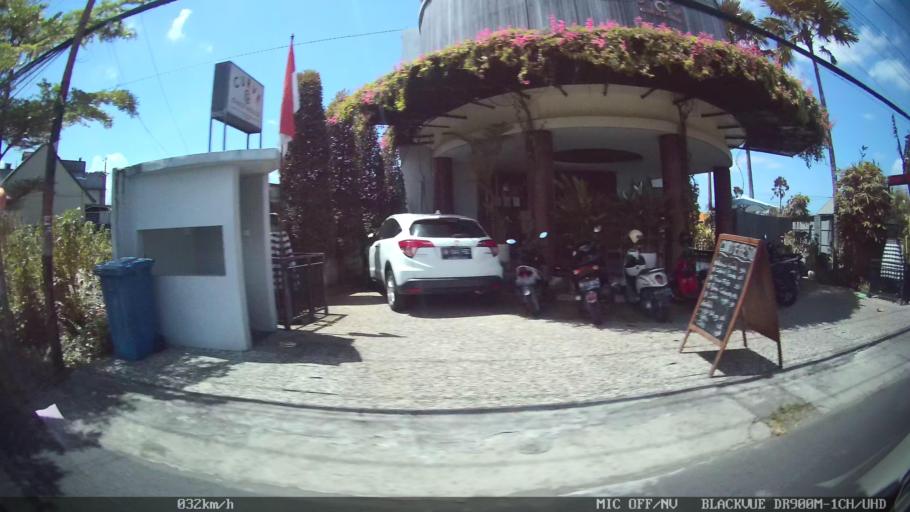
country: ID
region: Bali
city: Banjar Gunungpande
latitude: -8.6507
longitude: 115.1611
